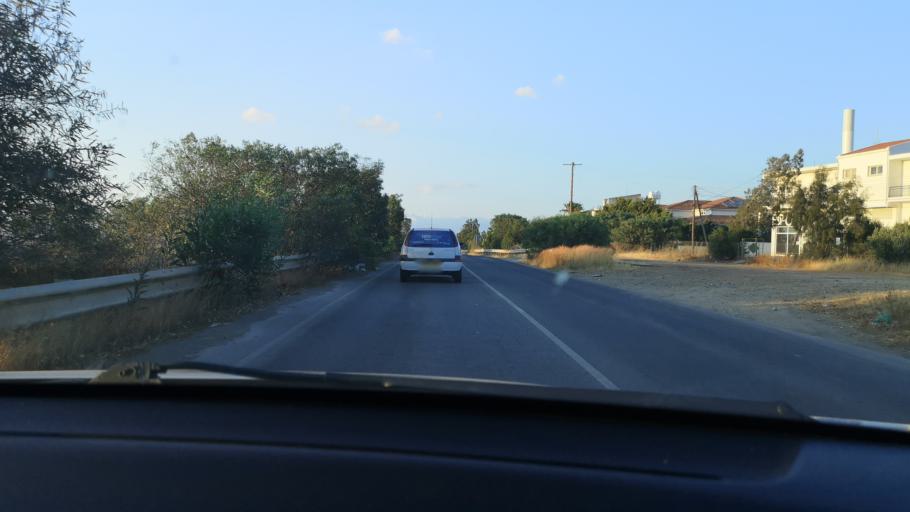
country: CY
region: Lefkosia
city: Kato Deftera
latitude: 35.1189
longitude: 33.2882
